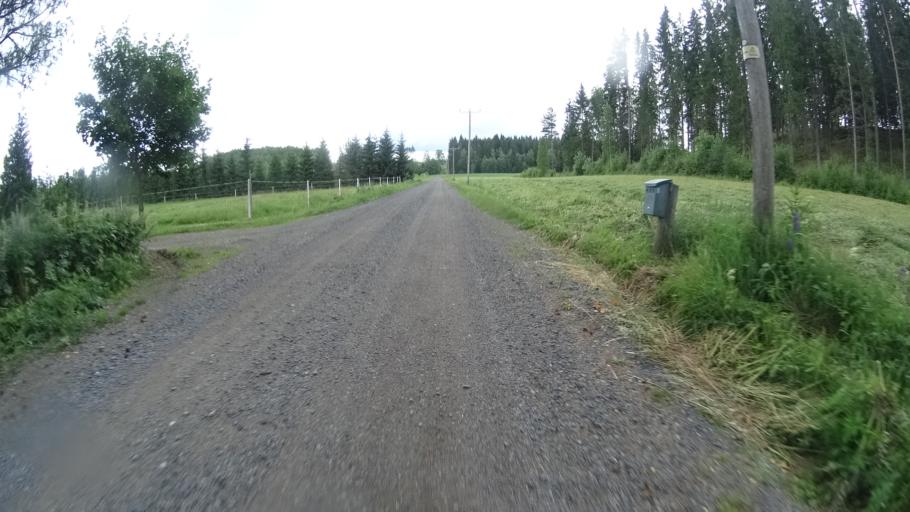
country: FI
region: Uusimaa
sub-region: Helsinki
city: Karkkila
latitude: 60.5868
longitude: 24.1648
